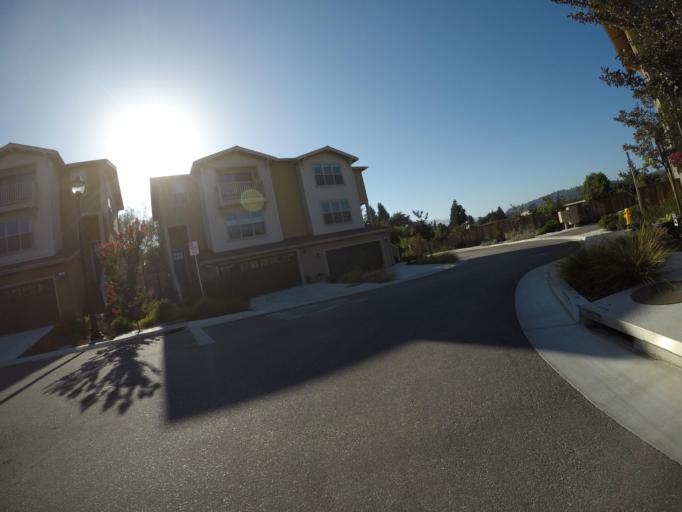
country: US
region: California
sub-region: Santa Cruz County
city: Scotts Valley
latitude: 37.0404
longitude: -122.0257
